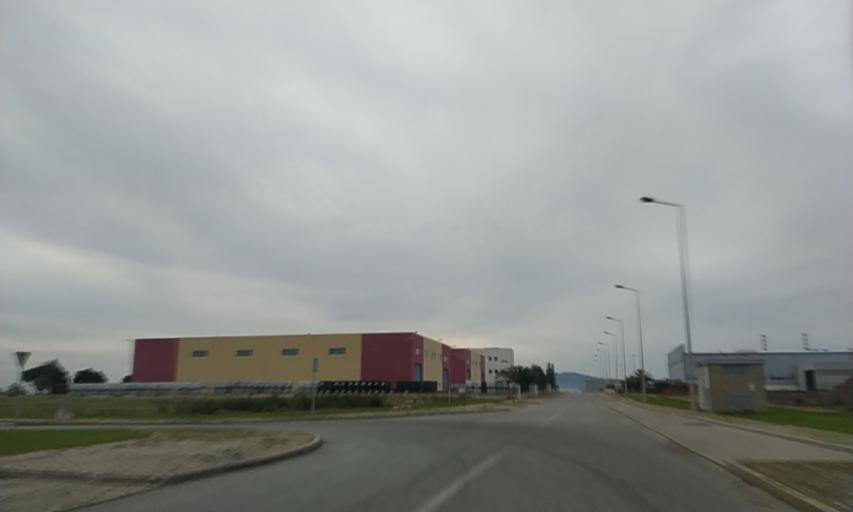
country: PT
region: Setubal
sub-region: Setubal
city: Setubal
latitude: 38.4974
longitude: -8.8242
